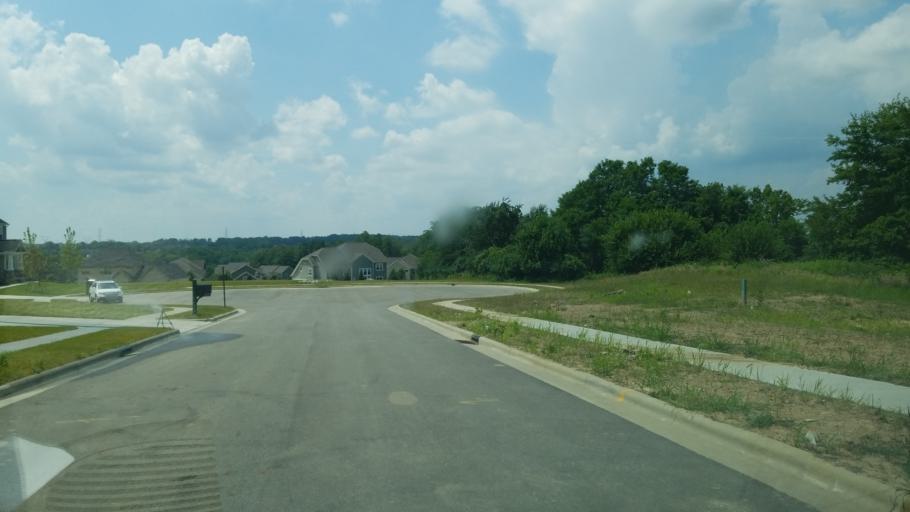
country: US
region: Ohio
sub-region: Delaware County
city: Lewis Center
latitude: 40.2088
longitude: -83.0489
